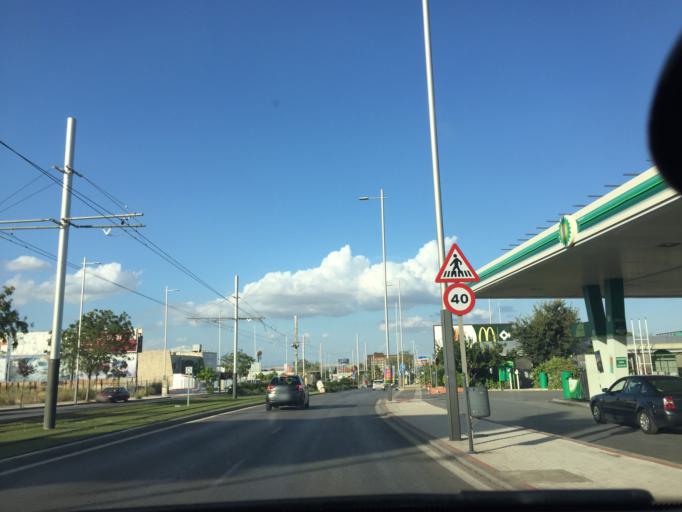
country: ES
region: Andalusia
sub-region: Provincia de Jaen
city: Jaen
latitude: 37.7886
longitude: -3.7822
